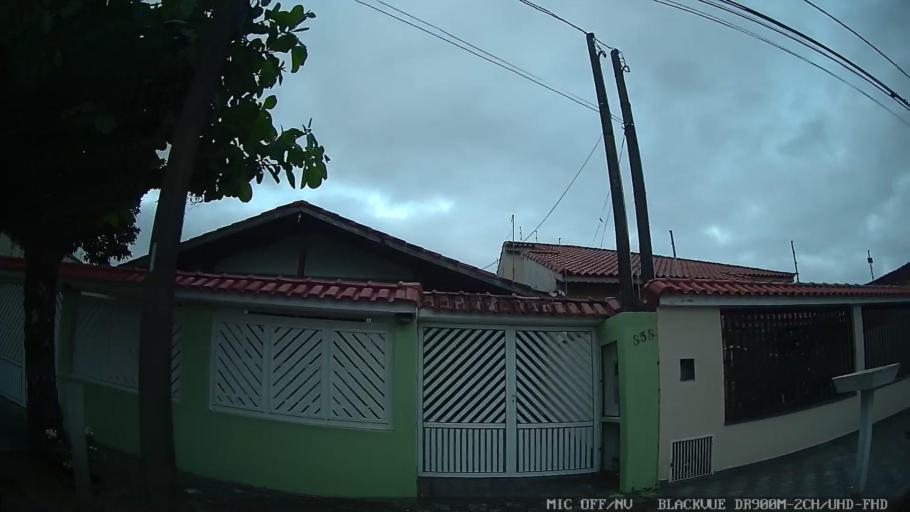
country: BR
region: Sao Paulo
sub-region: Peruibe
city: Peruibe
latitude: -24.3037
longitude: -46.9847
